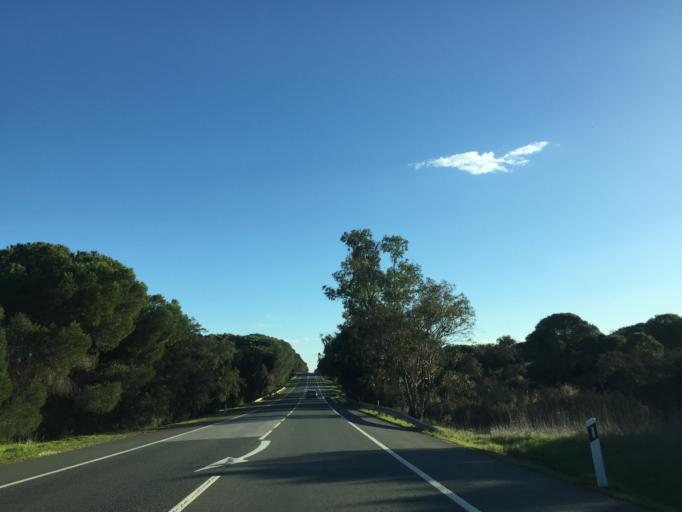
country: PT
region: Setubal
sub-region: Grandola
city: Grandola
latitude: 38.0894
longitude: -8.4180
